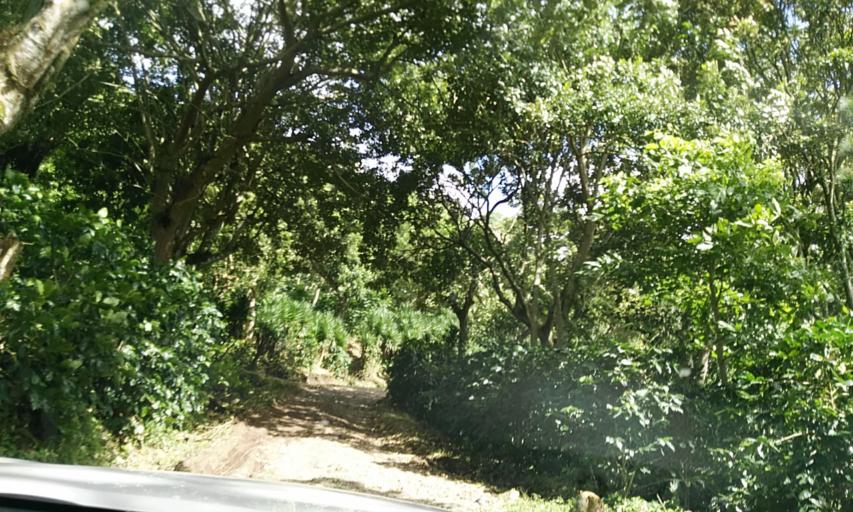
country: NI
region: Matagalpa
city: Matagalpa
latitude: 13.0125
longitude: -85.8775
